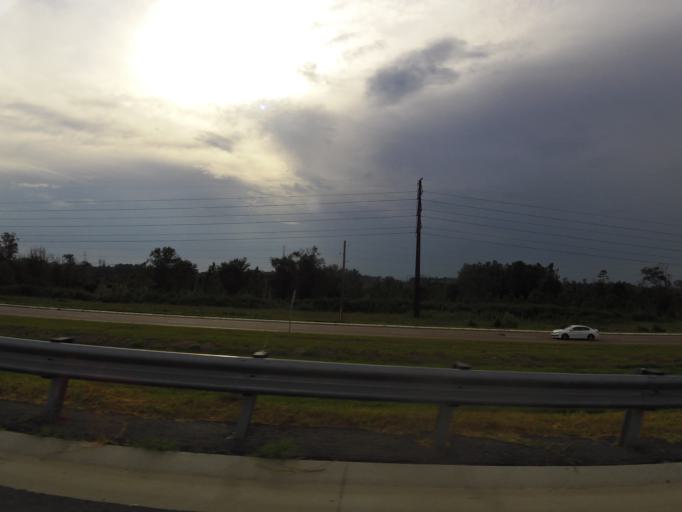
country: US
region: Florida
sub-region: Clay County
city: Middleburg
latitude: 30.1175
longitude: -81.8312
